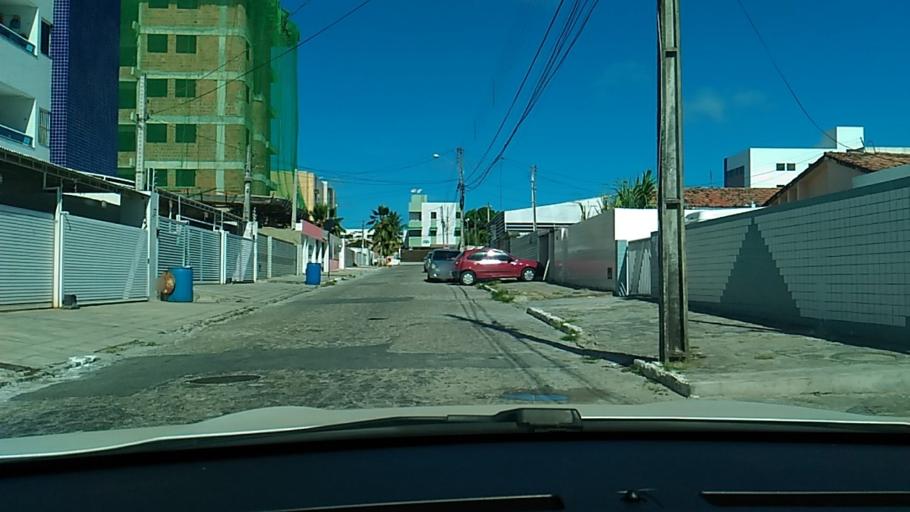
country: BR
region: Paraiba
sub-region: Joao Pessoa
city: Joao Pessoa
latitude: -7.1502
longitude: -34.8398
